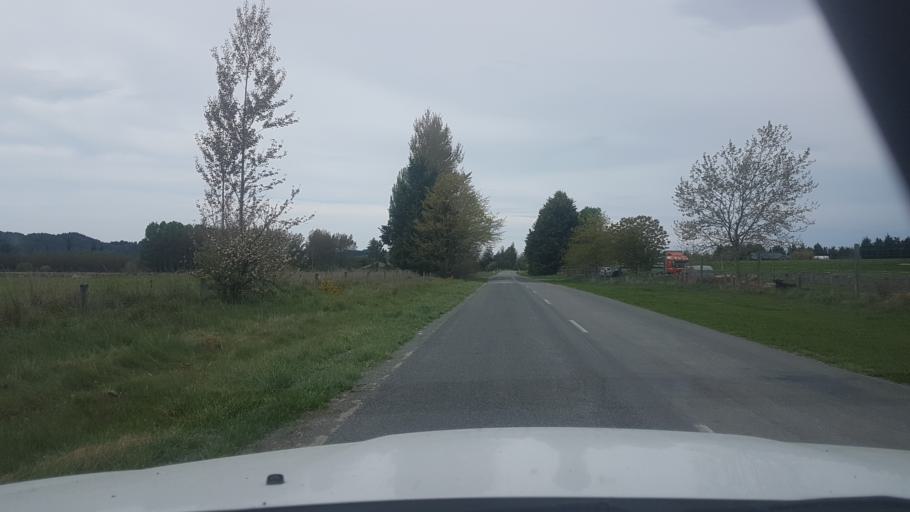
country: NZ
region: Canterbury
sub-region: Timaru District
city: Pleasant Point
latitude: -44.0784
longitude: 171.1760
